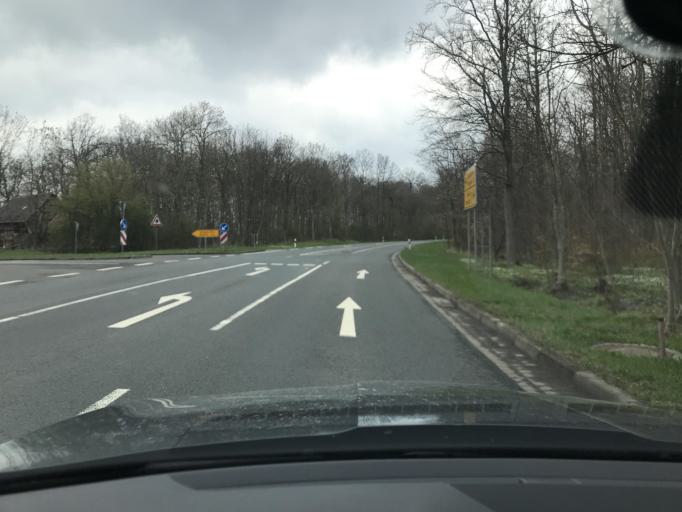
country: DE
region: Saxony-Anhalt
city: Harzgerode
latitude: 51.6225
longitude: 11.1514
